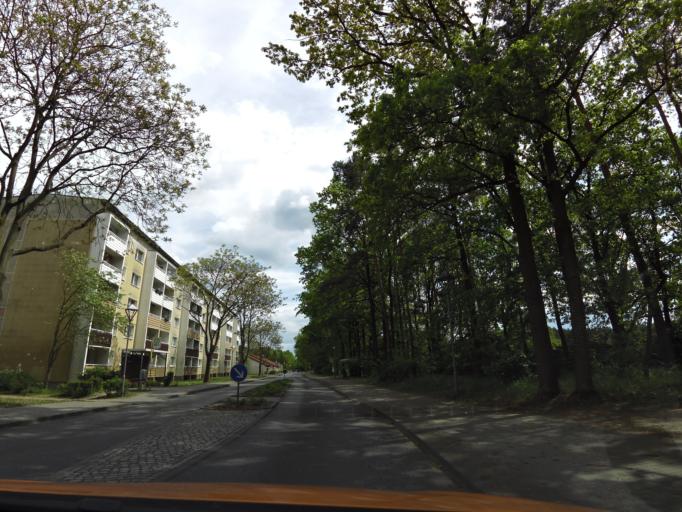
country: DE
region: Brandenburg
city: Michendorf
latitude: 52.2876
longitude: 12.9913
